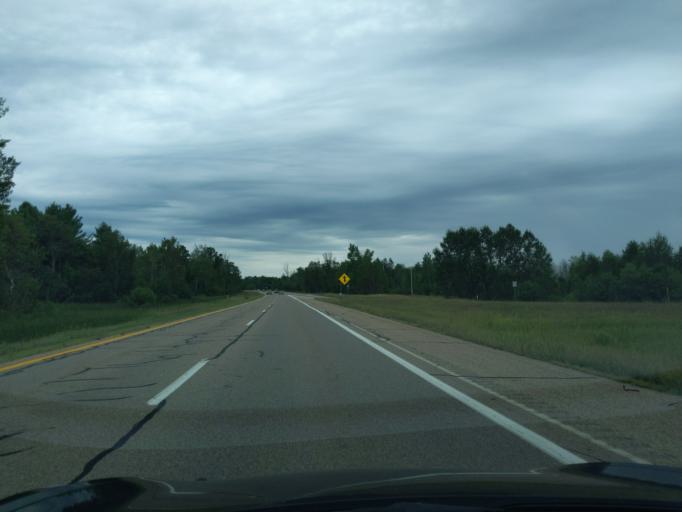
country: US
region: Michigan
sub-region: Roscommon County
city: Houghton Lake
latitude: 44.2678
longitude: -84.8031
